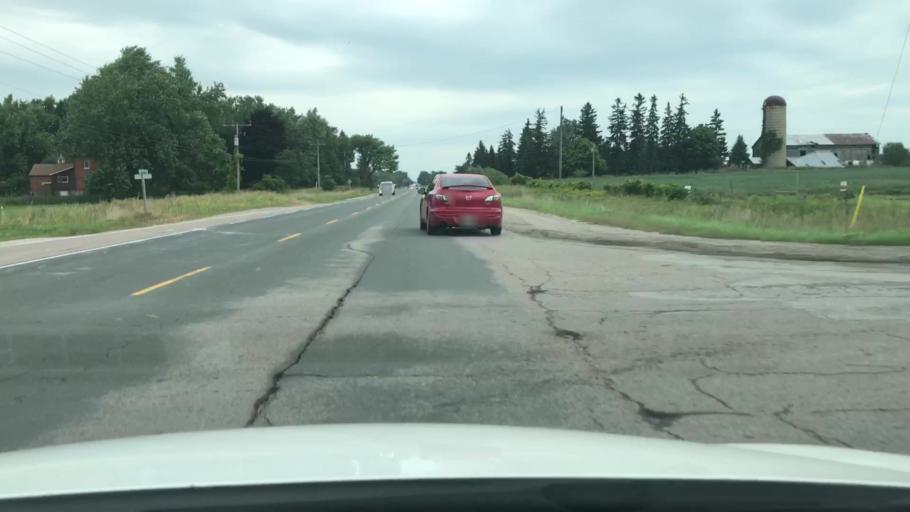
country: CA
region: Ontario
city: Innisfil
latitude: 44.3127
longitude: -79.6162
